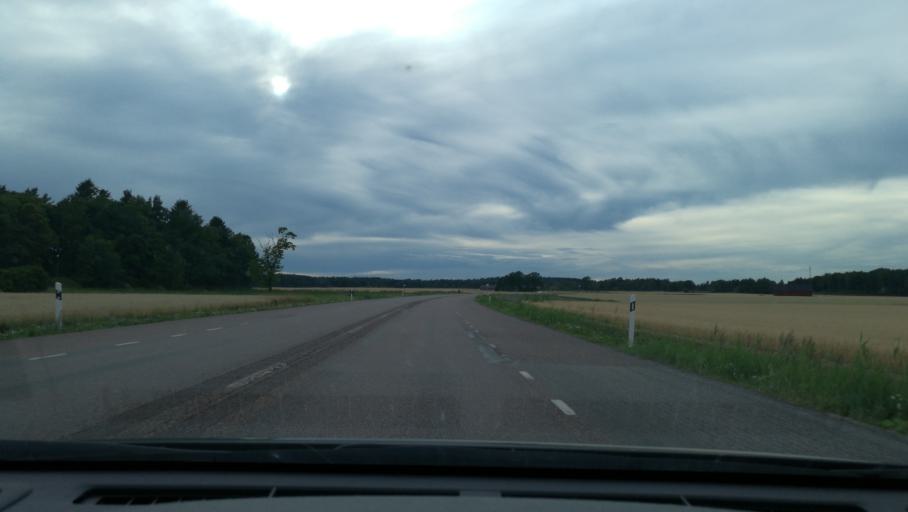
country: SE
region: Vaestmanland
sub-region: Kopings Kommun
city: Koping
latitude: 59.4585
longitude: 16.0104
